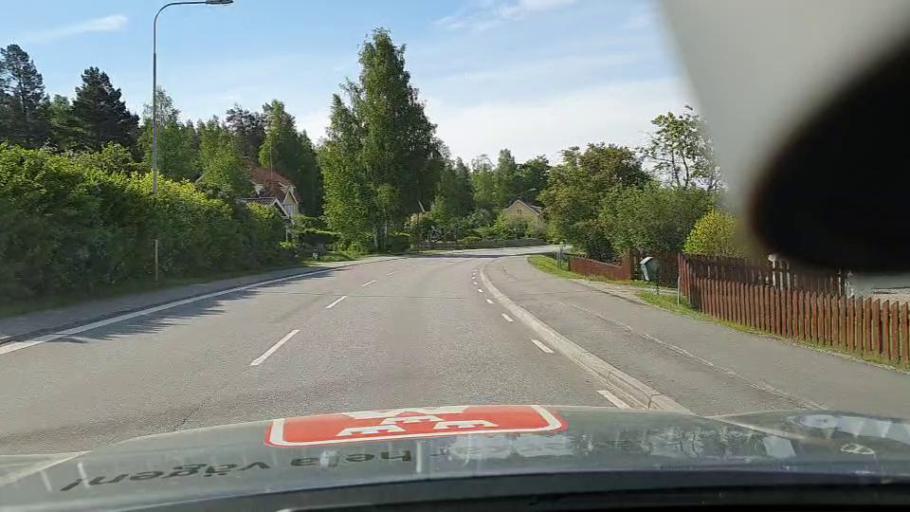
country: SE
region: Soedermanland
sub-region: Eskilstuna Kommun
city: Arla
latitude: 59.2885
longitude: 16.6774
